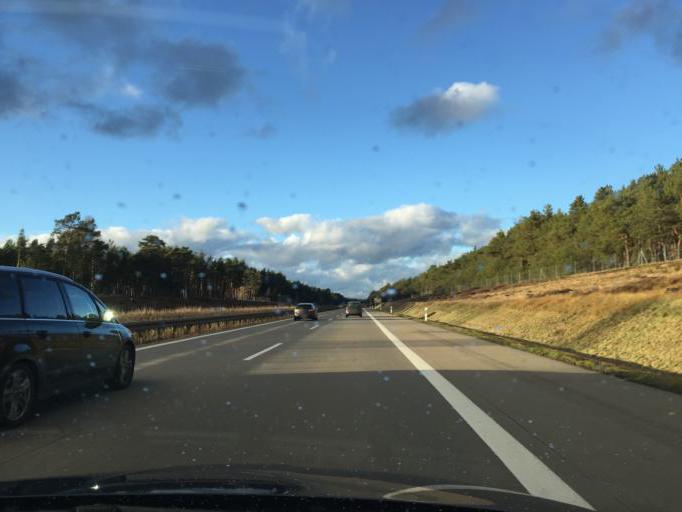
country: DE
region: Brandenburg
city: Kasel-Golzig
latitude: 51.9202
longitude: 13.7816
